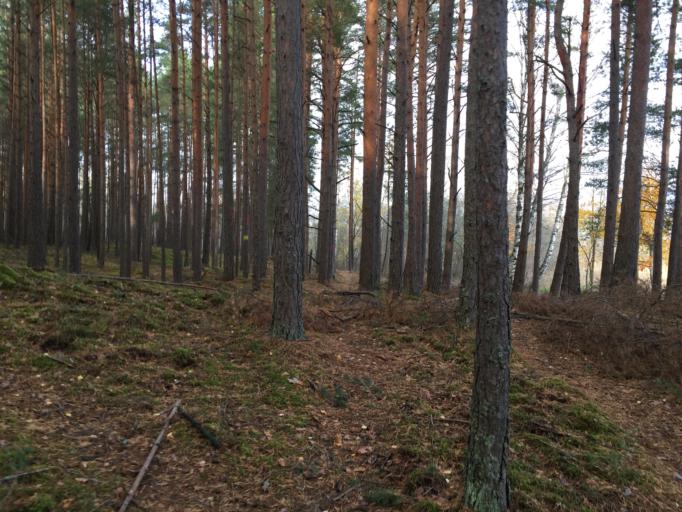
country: LV
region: Carnikava
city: Carnikava
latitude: 57.1482
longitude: 24.2633
